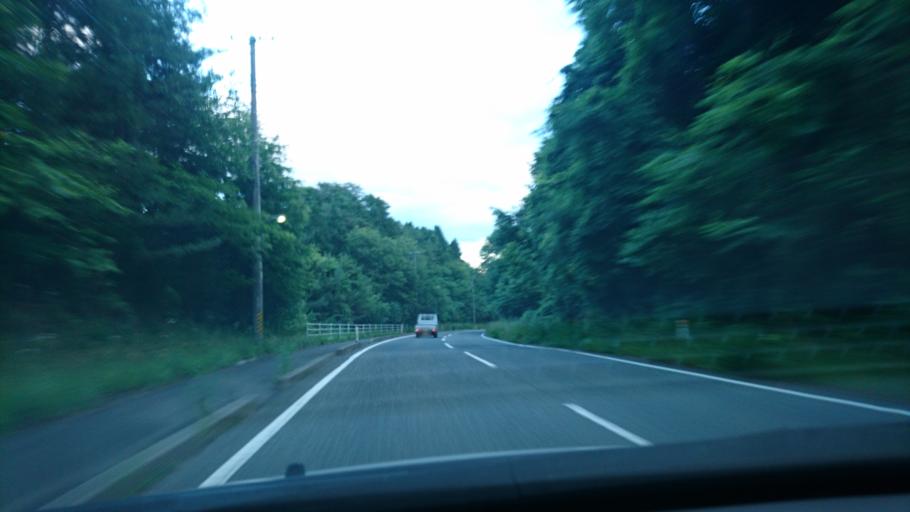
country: JP
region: Iwate
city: Ichinoseki
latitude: 38.7838
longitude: 141.0573
